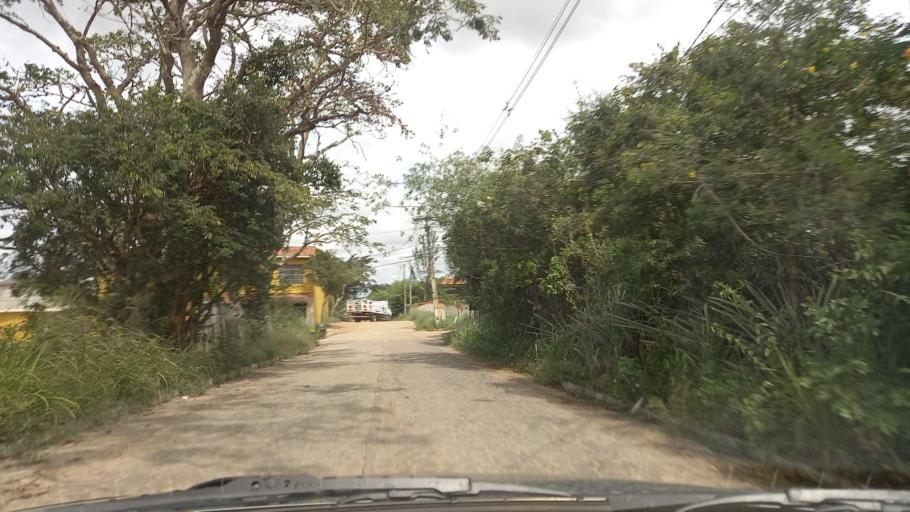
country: BR
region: Pernambuco
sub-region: Gravata
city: Gravata
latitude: -8.1846
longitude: -35.5802
